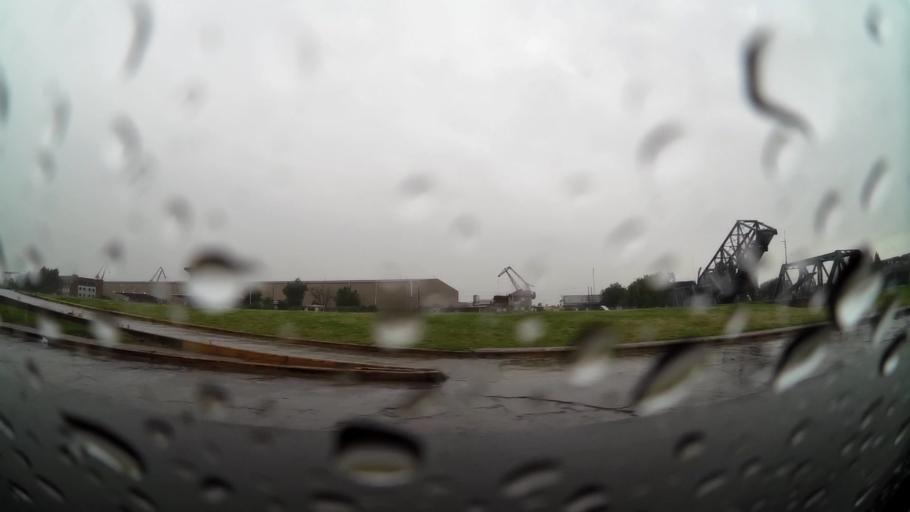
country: AR
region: Buenos Aires
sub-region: Partido de Avellaneda
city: Avellaneda
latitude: -34.6473
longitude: -58.3617
